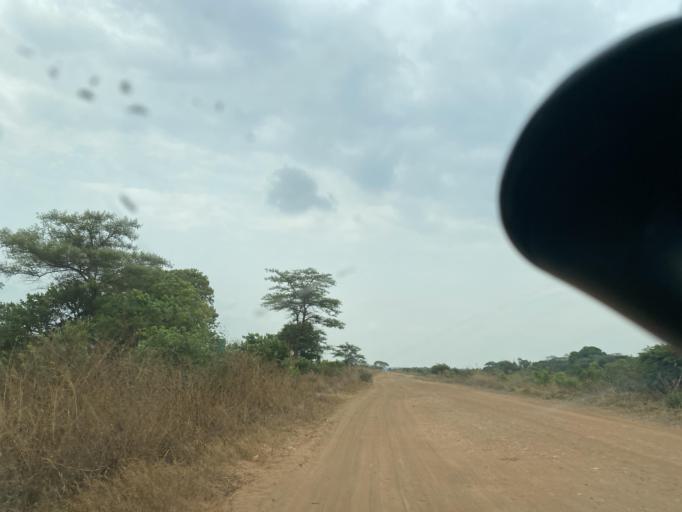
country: ZM
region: Lusaka
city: Lusaka
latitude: -15.2248
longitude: 28.3366
